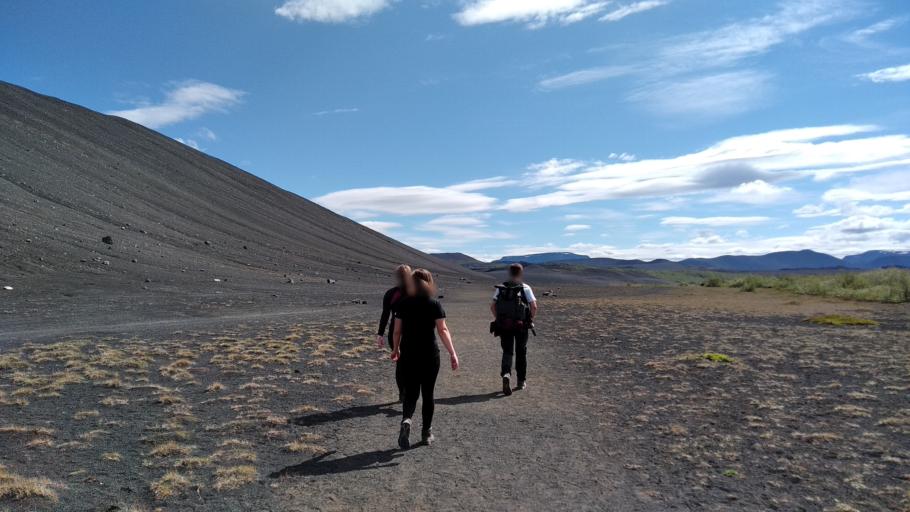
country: IS
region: Northeast
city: Laugar
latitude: 65.5989
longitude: -16.8864
